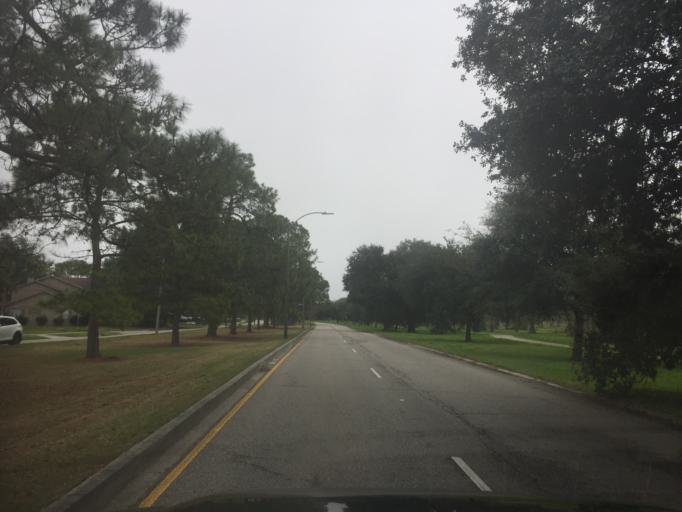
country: US
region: Louisiana
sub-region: Orleans Parish
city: New Orleans
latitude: 30.0185
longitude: -90.0952
